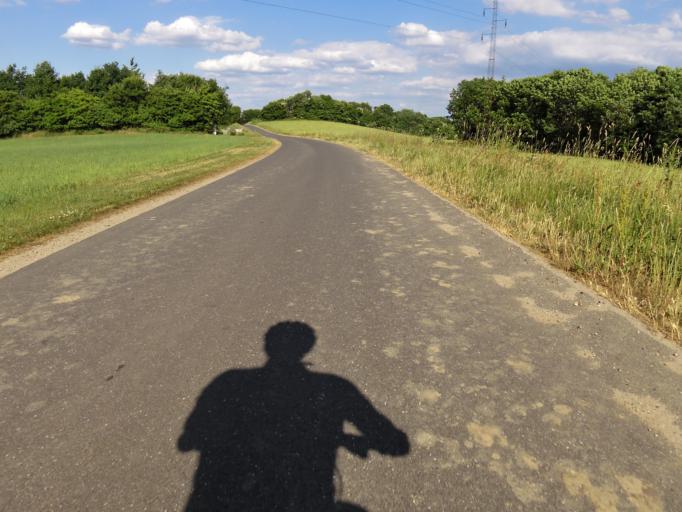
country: DK
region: Central Jutland
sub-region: Holstebro Kommune
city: Vinderup
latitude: 56.4552
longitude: 8.8380
